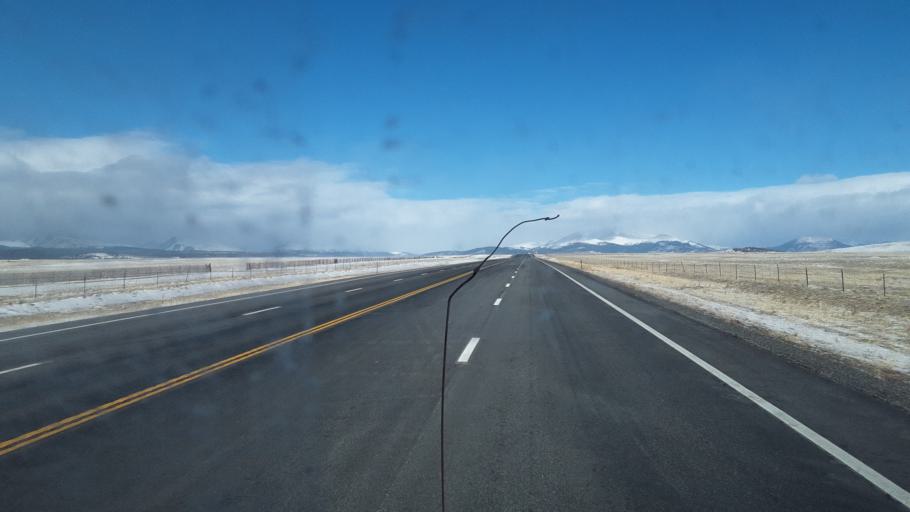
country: US
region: Colorado
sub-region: Park County
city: Fairplay
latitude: 39.1378
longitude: -105.9961
